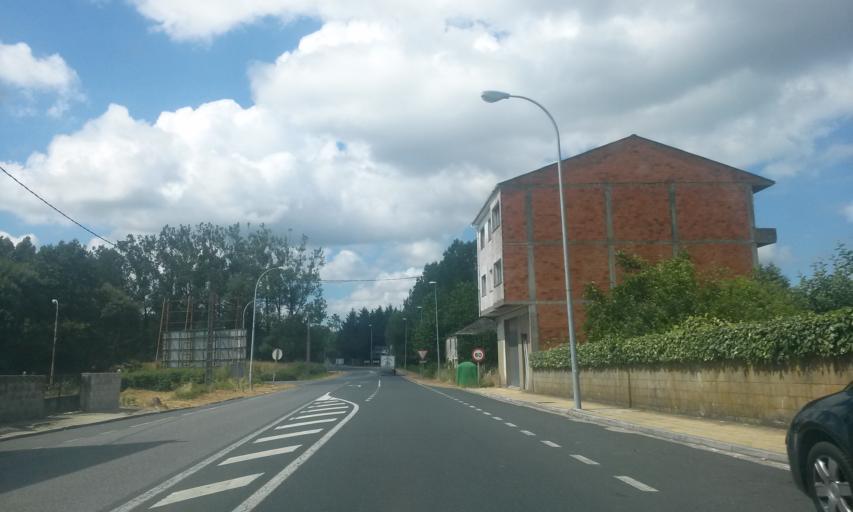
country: ES
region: Galicia
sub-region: Provincia de Lugo
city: Rabade
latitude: 43.1267
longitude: -7.6226
